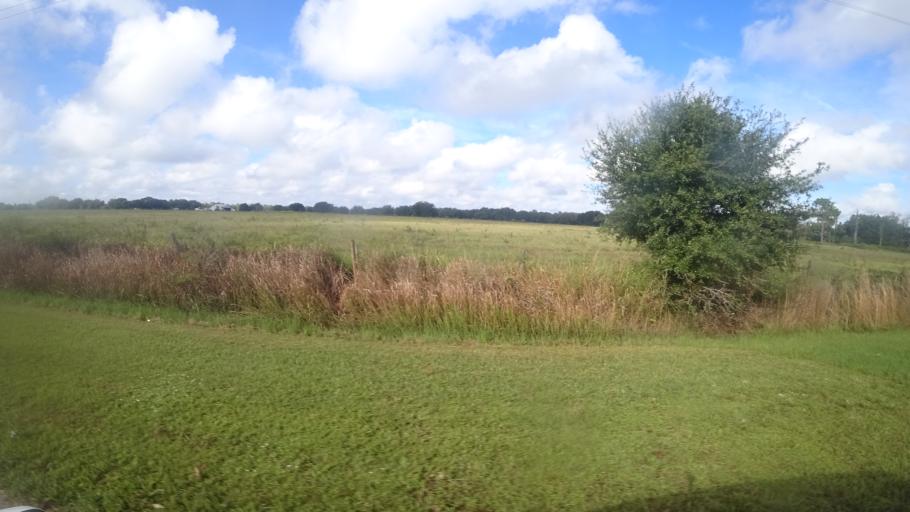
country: US
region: Florida
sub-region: Hillsborough County
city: Sun City Center
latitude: 27.5954
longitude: -82.3866
